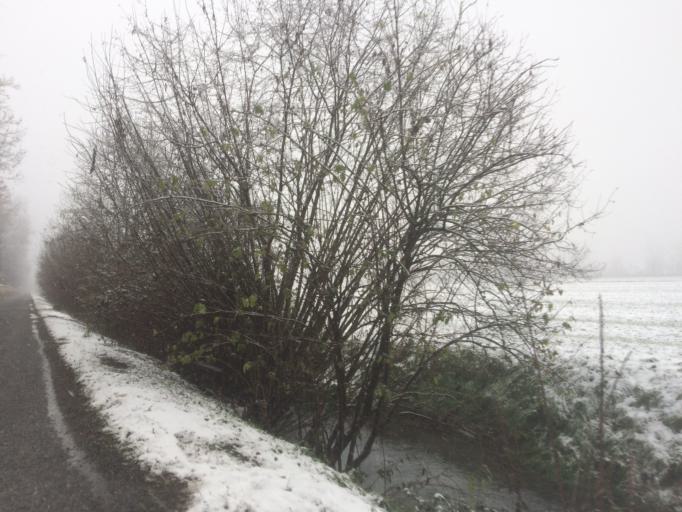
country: IT
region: Piedmont
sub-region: Provincia di Cuneo
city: Racconigi
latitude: 44.7782
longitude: 7.6689
